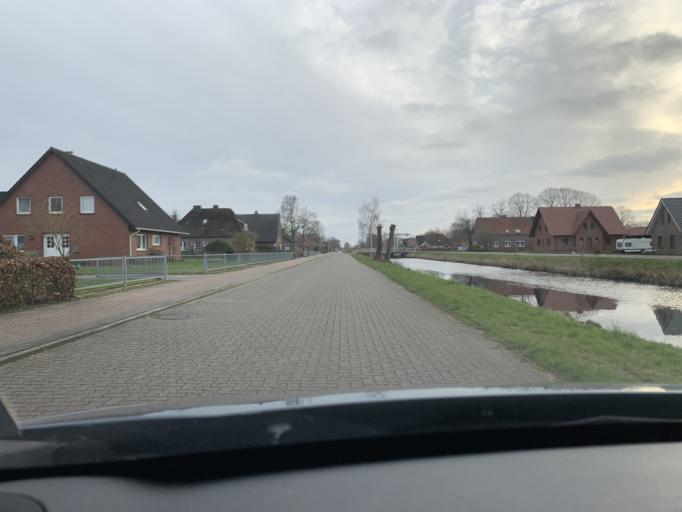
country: DE
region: Lower Saxony
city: Schwerinsdorf
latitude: 53.2726
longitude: 7.6990
